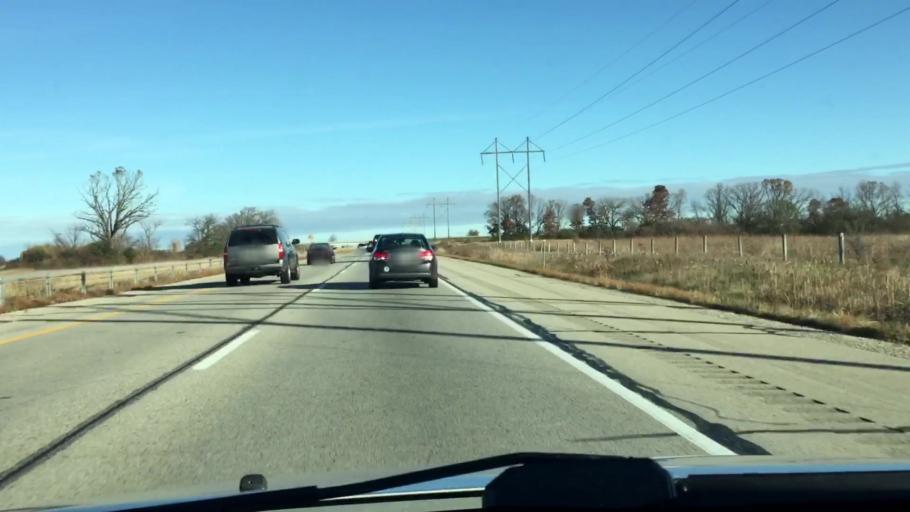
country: US
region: Wisconsin
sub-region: Fond du Lac County
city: Rosendale
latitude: 43.8662
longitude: -88.5839
